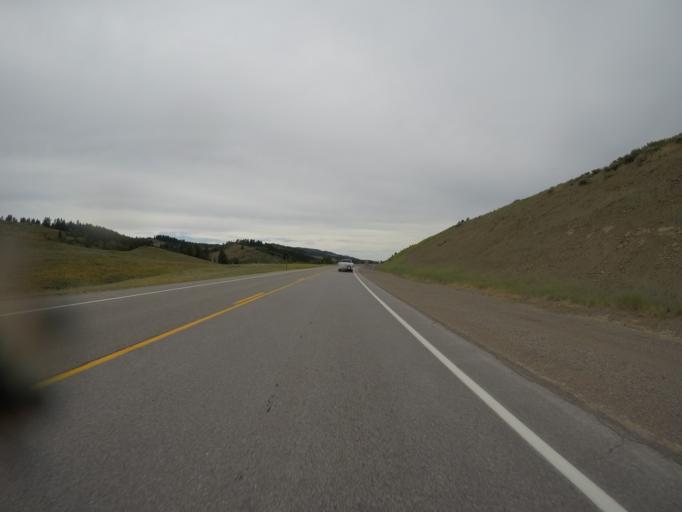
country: US
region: Wyoming
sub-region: Lincoln County
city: Afton
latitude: 42.5273
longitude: -110.8974
